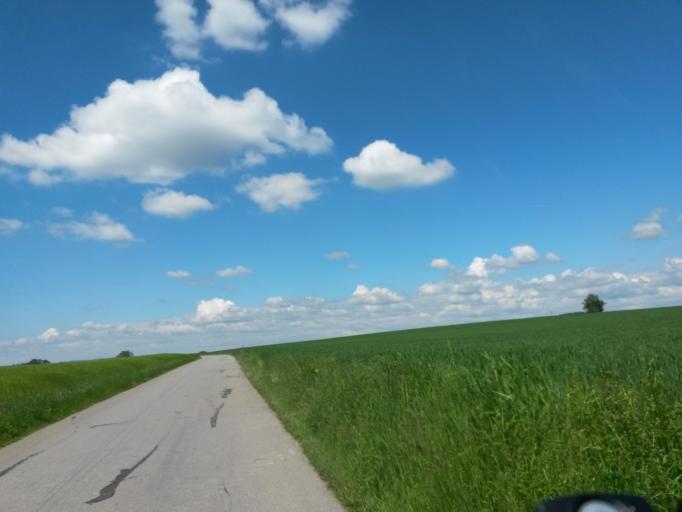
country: DE
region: Baden-Wuerttemberg
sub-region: Tuebingen Region
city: Bad Waldsee
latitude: 47.9348
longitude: 9.7364
